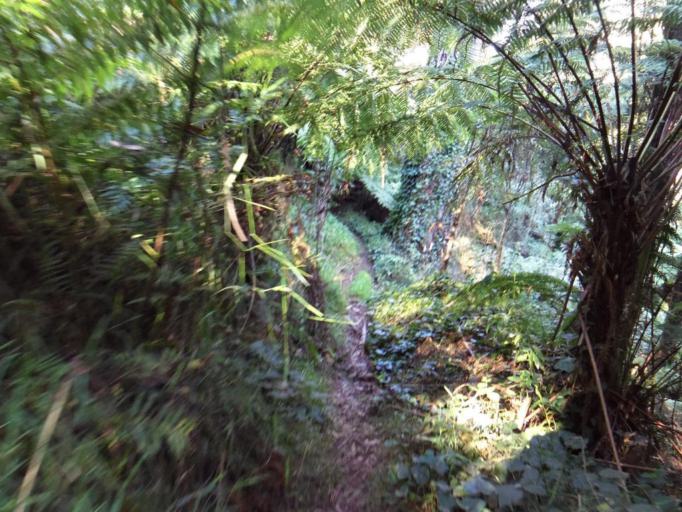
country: AU
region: Victoria
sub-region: Yarra Ranges
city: Monbulk
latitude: -37.8750
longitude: 145.4023
